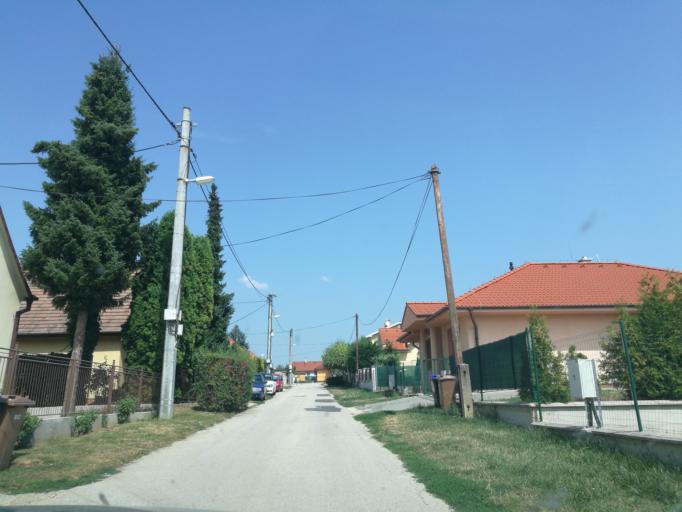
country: SK
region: Nitriansky
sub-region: Okres Nitra
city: Nitra
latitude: 48.2933
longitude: 18.1314
